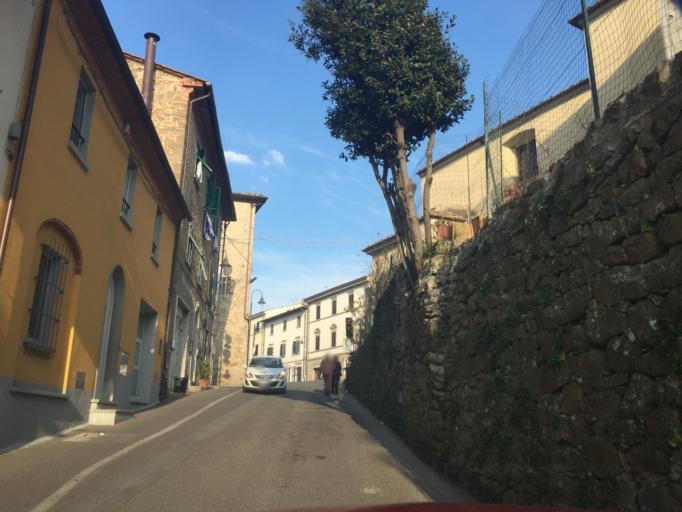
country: IT
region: Tuscany
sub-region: Province of Florence
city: Vinci
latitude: 43.7841
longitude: 10.9240
